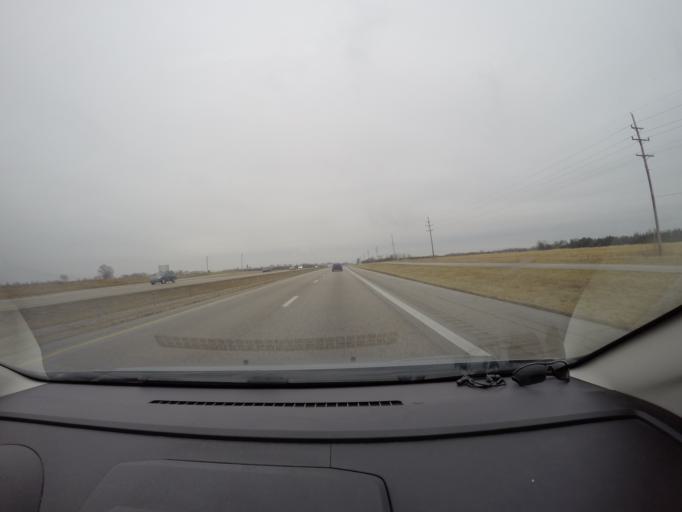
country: US
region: Missouri
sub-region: Montgomery County
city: Montgomery City
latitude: 38.8844
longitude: -91.4037
